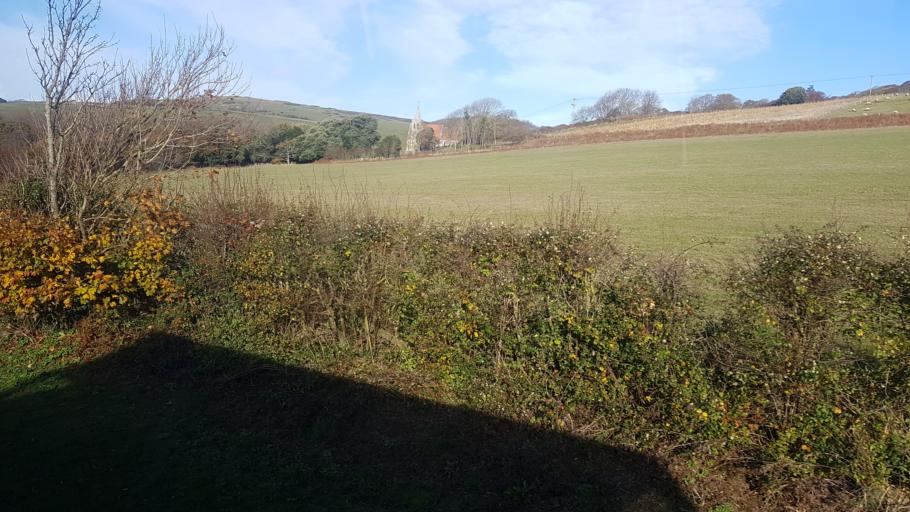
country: GB
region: England
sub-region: Isle of Wight
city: Shalfleet
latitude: 50.6556
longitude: -1.4423
